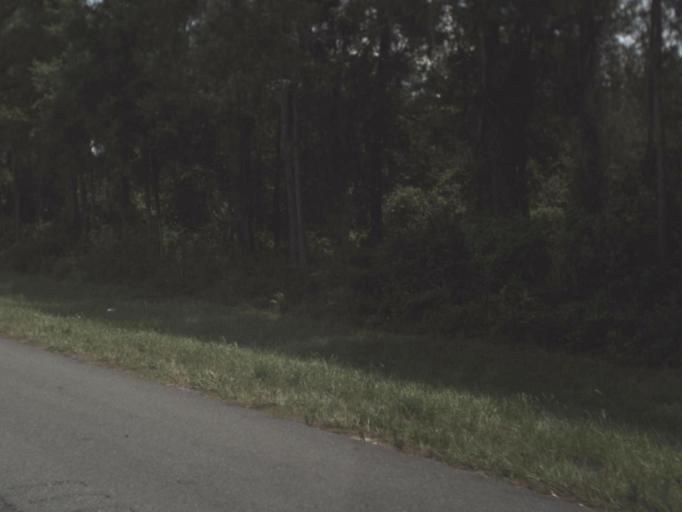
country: US
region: Florida
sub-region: Hamilton County
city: Jasper
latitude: 30.4097
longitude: -82.8926
